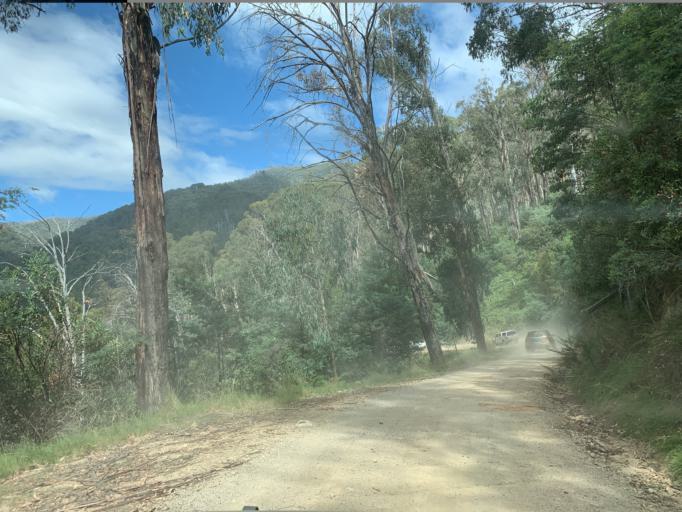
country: AU
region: Victoria
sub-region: Mansfield
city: Mansfield
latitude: -37.0998
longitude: 146.4994
